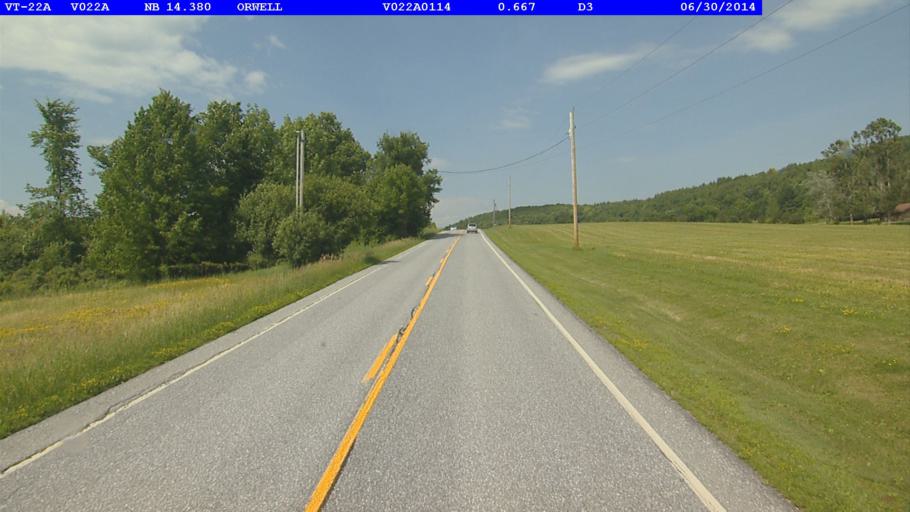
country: US
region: New York
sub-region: Essex County
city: Ticonderoga
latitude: 43.7668
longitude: -73.3101
